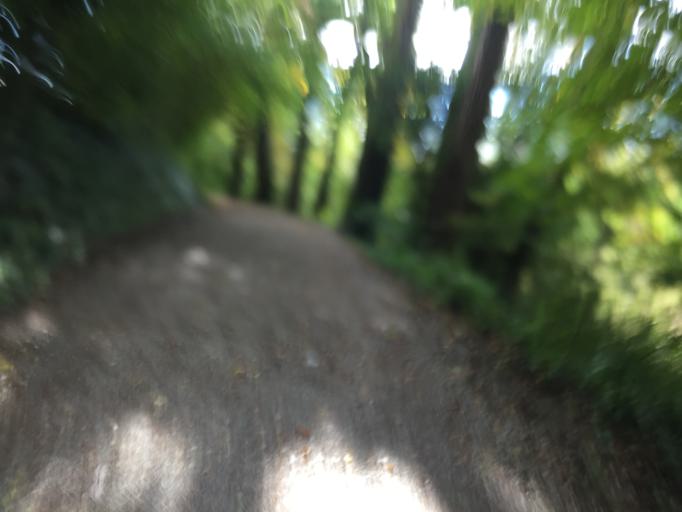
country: CH
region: Bern
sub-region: Bern-Mittelland District
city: Muri
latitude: 46.9215
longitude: 7.4970
